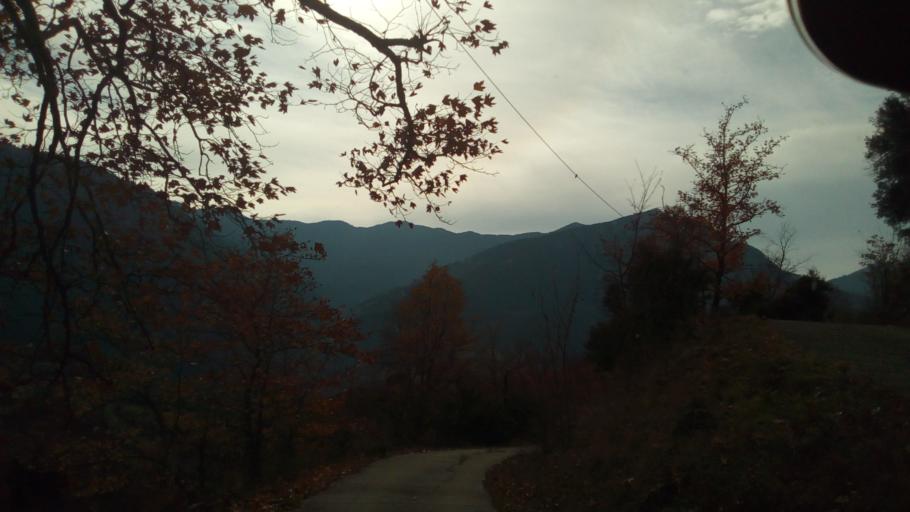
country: GR
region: West Greece
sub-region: Nomos Aitolias kai Akarnanias
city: Thermo
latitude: 38.6837
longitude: 21.9041
